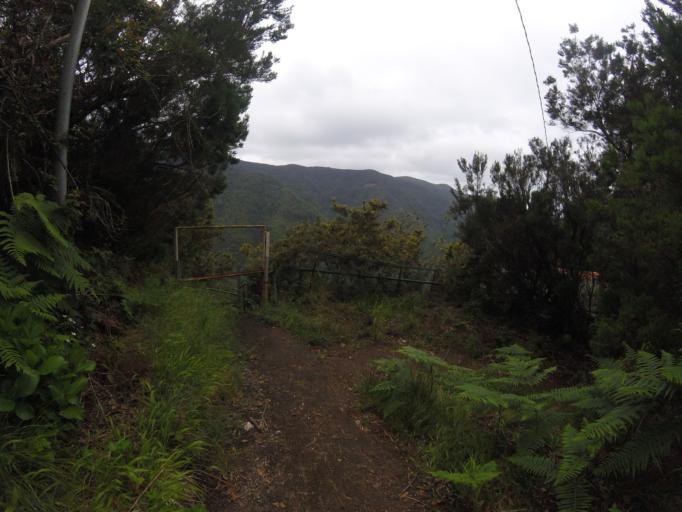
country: ES
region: Canary Islands
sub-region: Provincia de Santa Cruz de Tenerife
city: Tegueste
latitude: 28.5437
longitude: -16.2818
